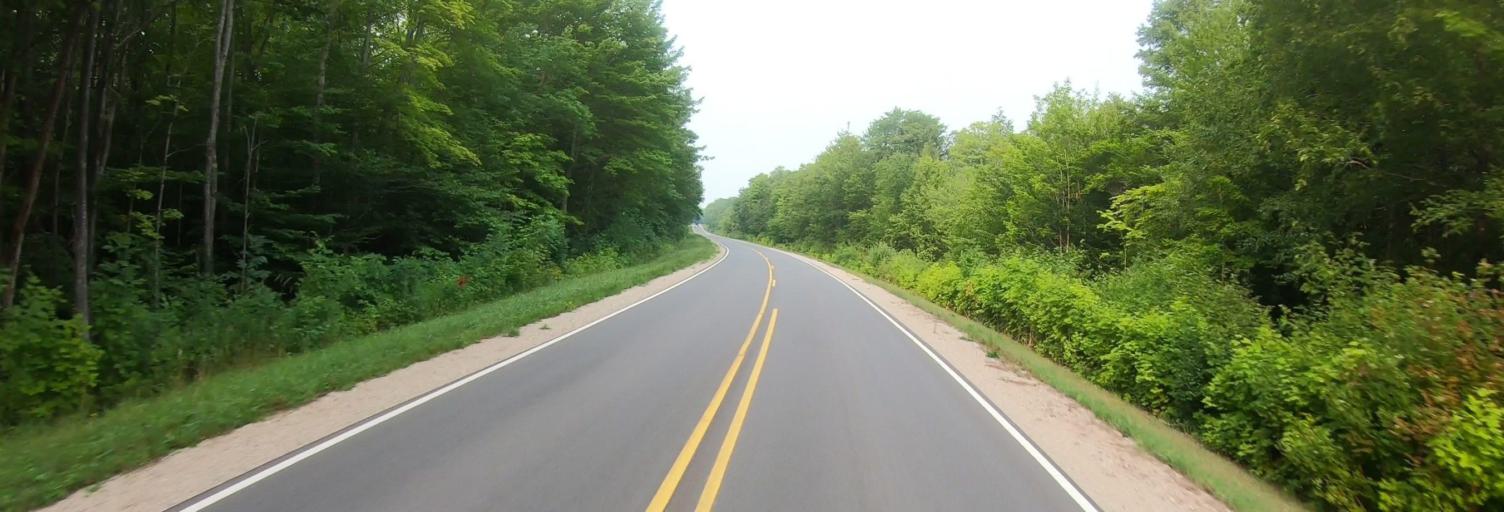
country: US
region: Michigan
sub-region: Luce County
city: Newberry
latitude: 46.4853
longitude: -85.0497
